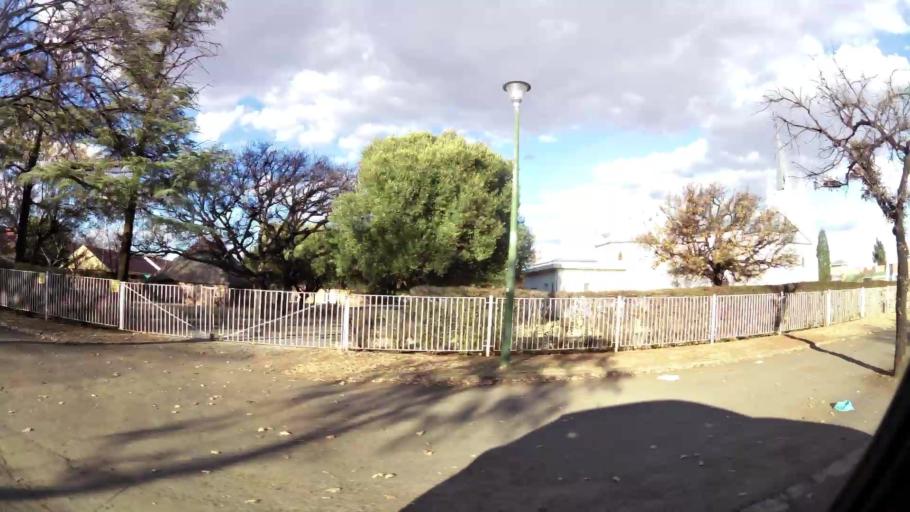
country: ZA
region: North-West
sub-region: Dr Kenneth Kaunda District Municipality
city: Potchefstroom
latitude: -26.7134
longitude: 27.0911
